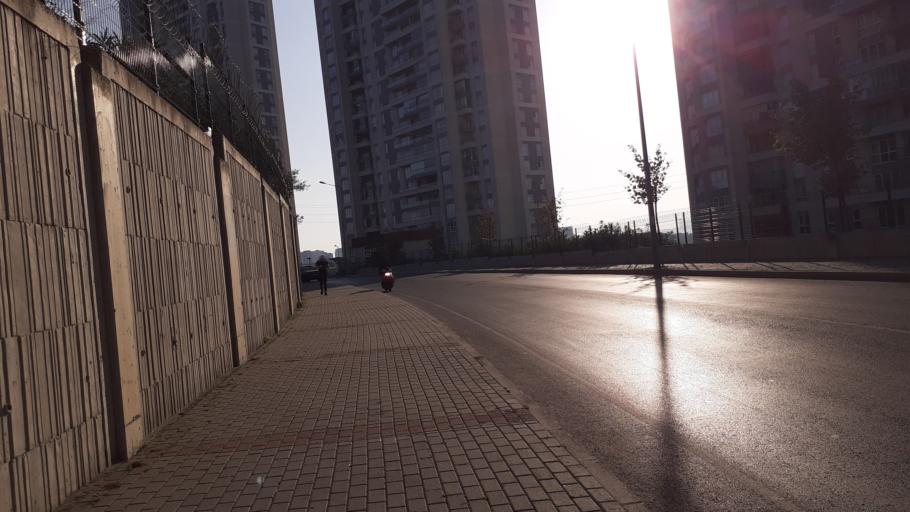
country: TR
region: Istanbul
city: Basaksehir
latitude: 41.0665
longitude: 28.7762
